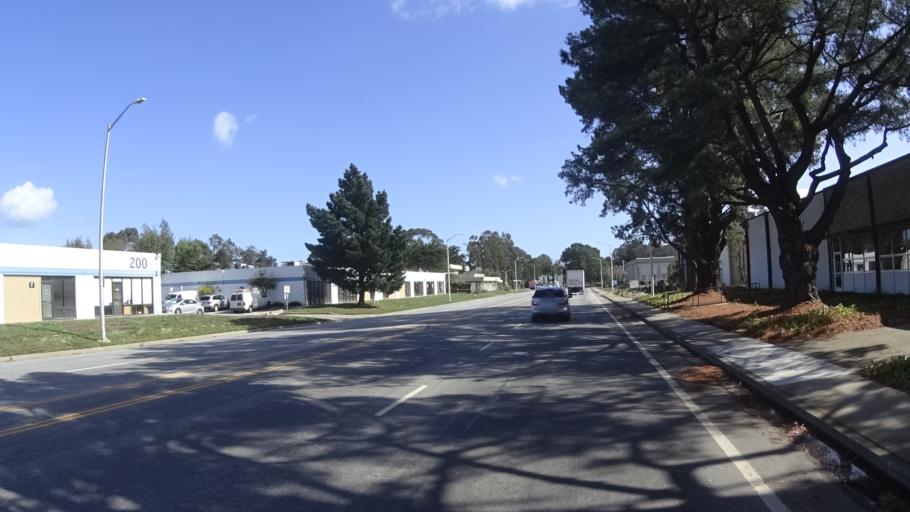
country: US
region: California
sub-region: San Mateo County
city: Brisbane
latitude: 37.6878
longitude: -122.4041
